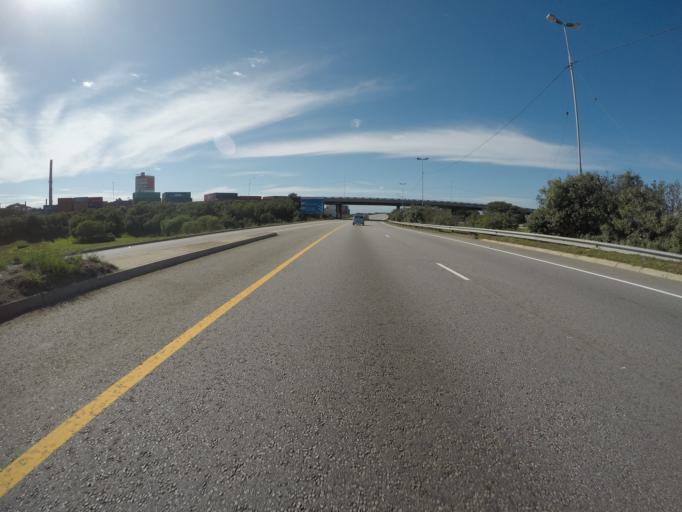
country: ZA
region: Eastern Cape
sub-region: Nelson Mandela Bay Metropolitan Municipality
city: Port Elizabeth
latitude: -33.9137
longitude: 25.6014
